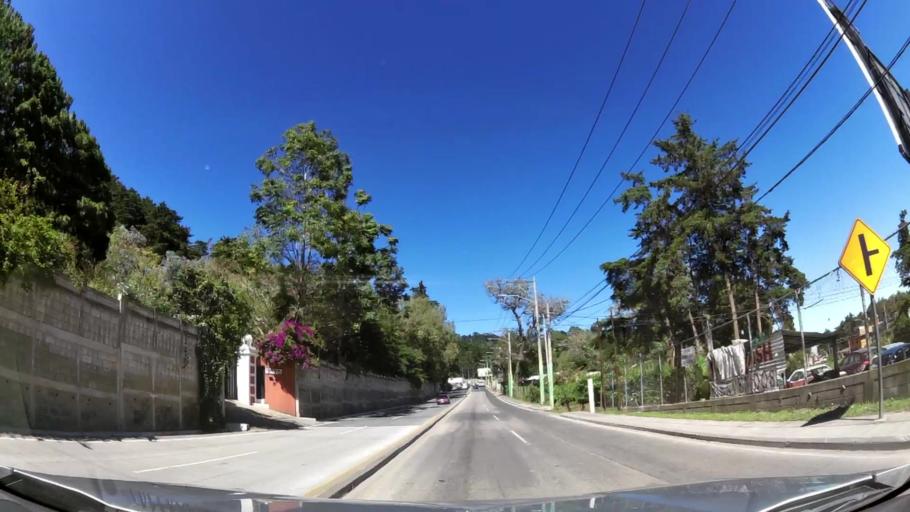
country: GT
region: Guatemala
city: San Jose Pinula
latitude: 14.5470
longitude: -90.4183
